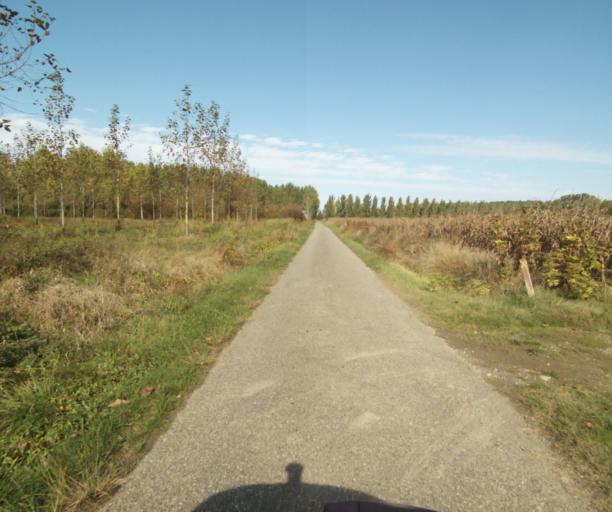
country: FR
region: Midi-Pyrenees
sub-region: Departement du Tarn-et-Garonne
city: Finhan
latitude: 43.9050
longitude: 1.2168
